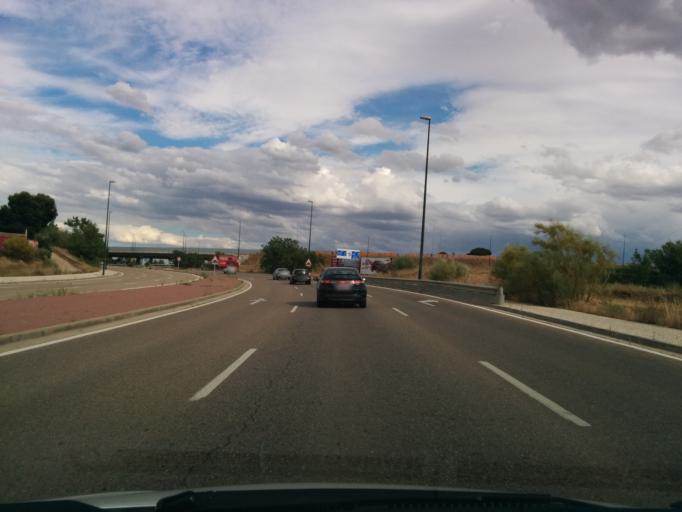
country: ES
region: Aragon
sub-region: Provincia de Zaragoza
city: Zaragoza
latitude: 41.6224
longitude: -0.8652
